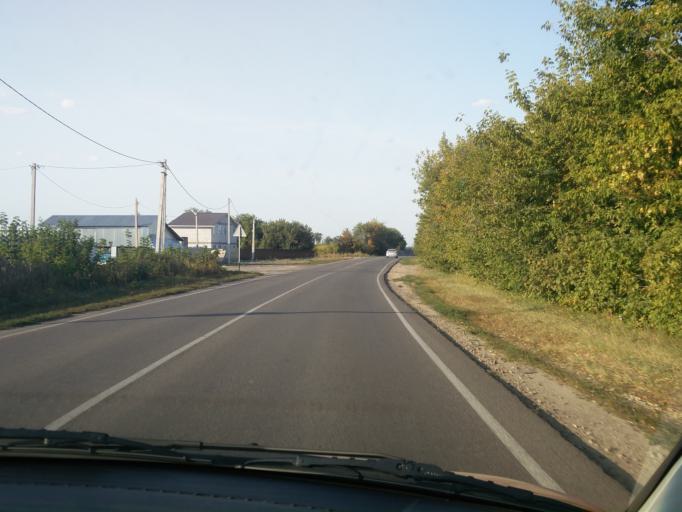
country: RU
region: Voronezj
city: Ramon'
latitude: 51.9188
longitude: 39.3207
